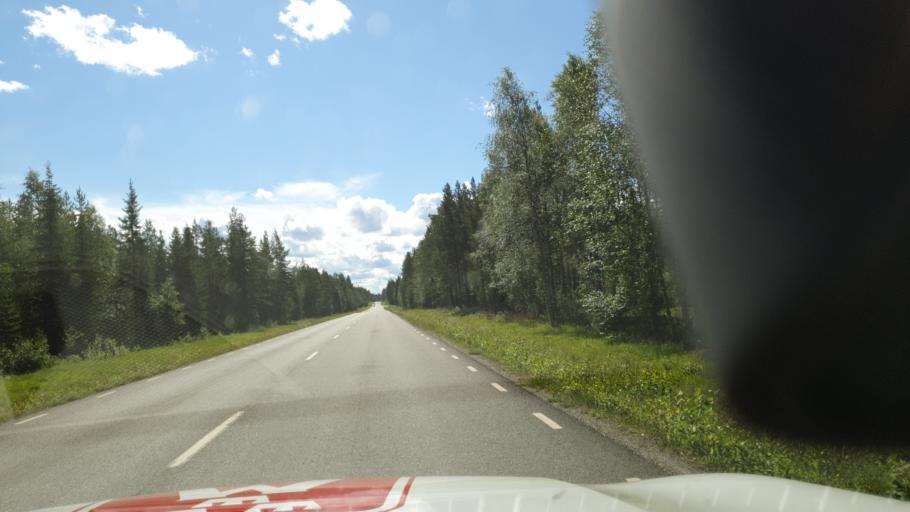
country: SE
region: Vaesterbotten
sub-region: Lycksele Kommun
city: Lycksele
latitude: 64.7257
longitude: 18.6822
